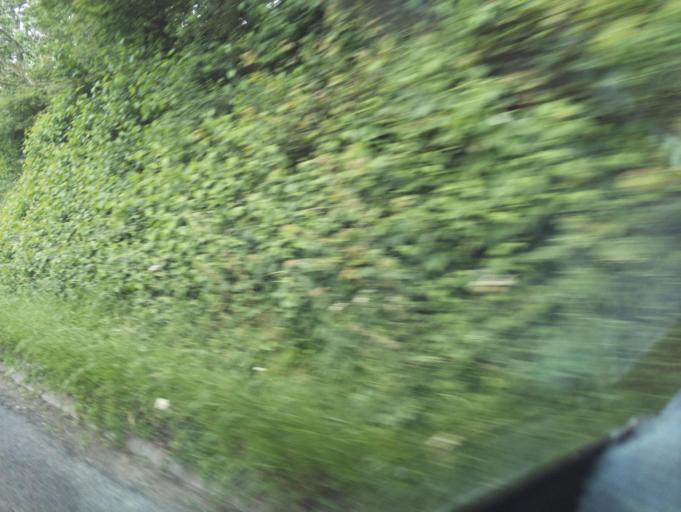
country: GB
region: England
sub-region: Bath and North East Somerset
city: Bath
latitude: 51.4096
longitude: -2.3957
